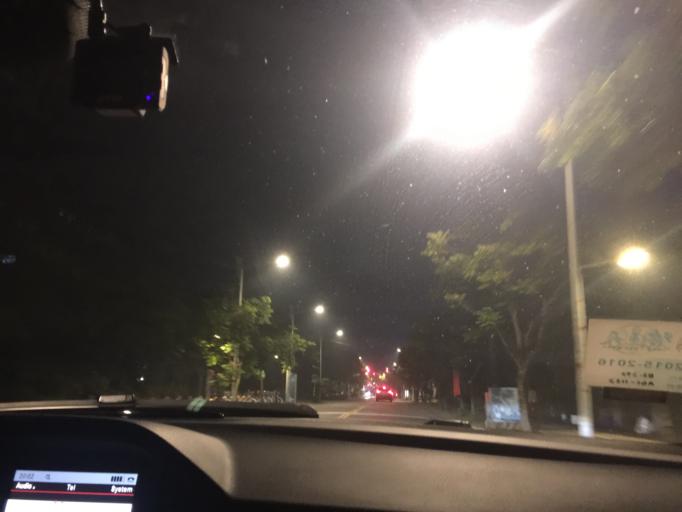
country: TW
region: Taiwan
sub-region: Taoyuan
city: Taoyuan
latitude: 24.9421
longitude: 121.3597
